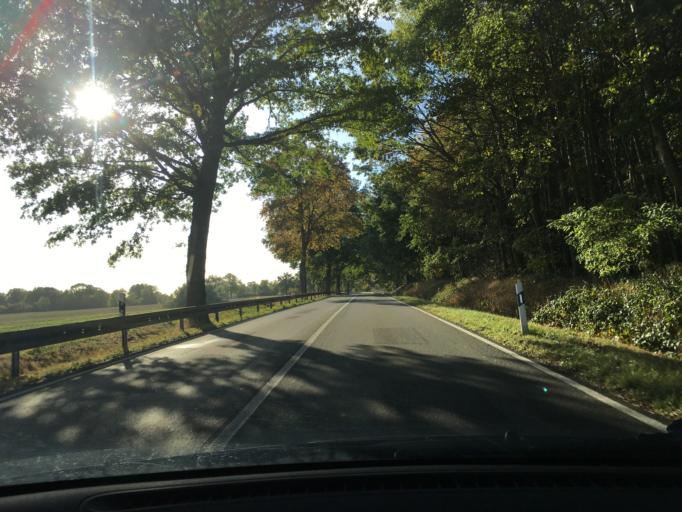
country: DE
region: Lower Saxony
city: Neu Darchau
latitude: 53.3840
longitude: 10.9004
